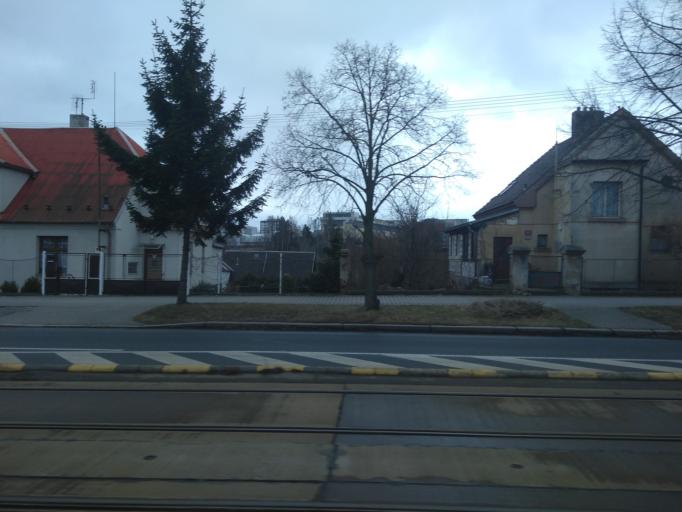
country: CZ
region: Plzensky
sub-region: Okres Plzen-Mesto
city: Pilsen
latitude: 49.7432
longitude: 13.3385
